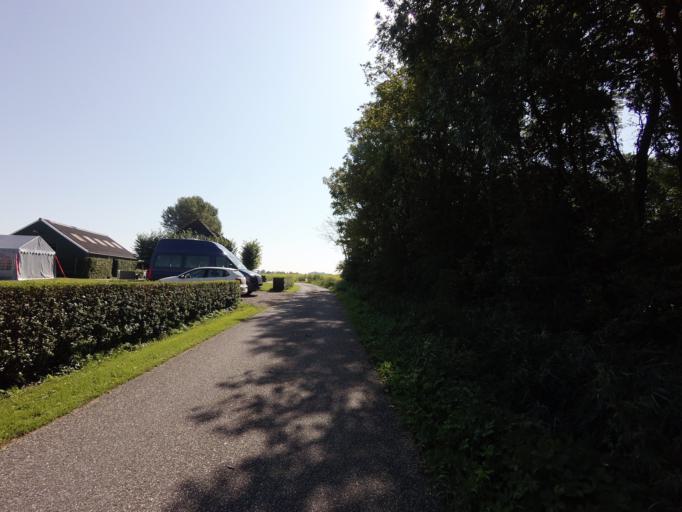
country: NL
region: Friesland
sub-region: Gemeente Dongeradeel
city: Holwerd
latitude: 53.3664
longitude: 5.9264
